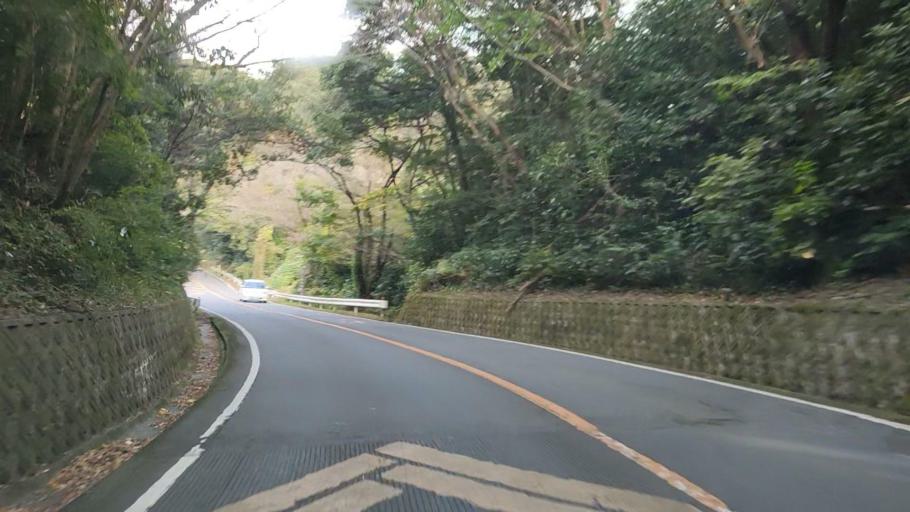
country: JP
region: Shizuoka
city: Shizuoka-shi
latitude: 34.9641
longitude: 138.4498
